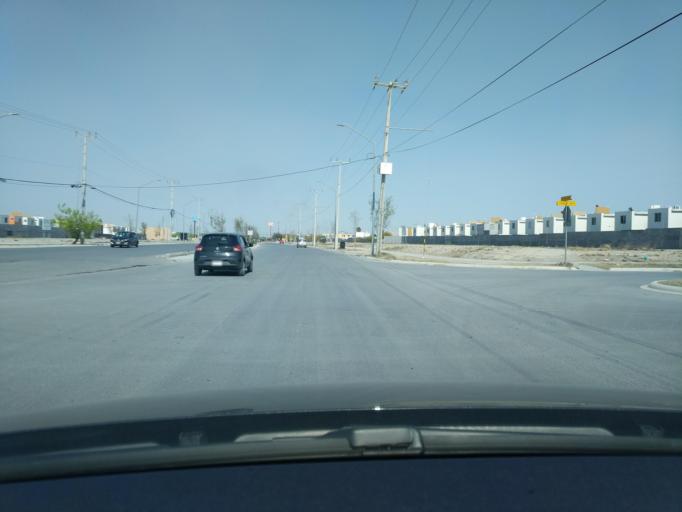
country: MX
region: Nuevo Leon
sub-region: Garcia
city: Los Parques
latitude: 25.7824
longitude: -100.4889
